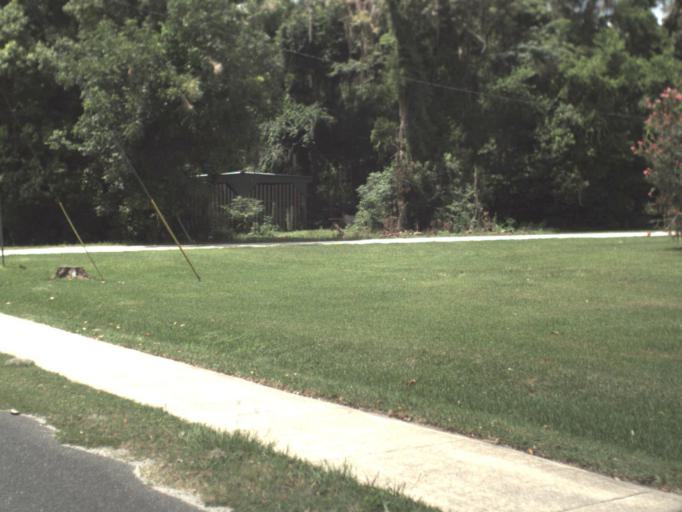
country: US
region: Florida
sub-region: Union County
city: Lake Butler
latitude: 29.9321
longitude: -82.4232
